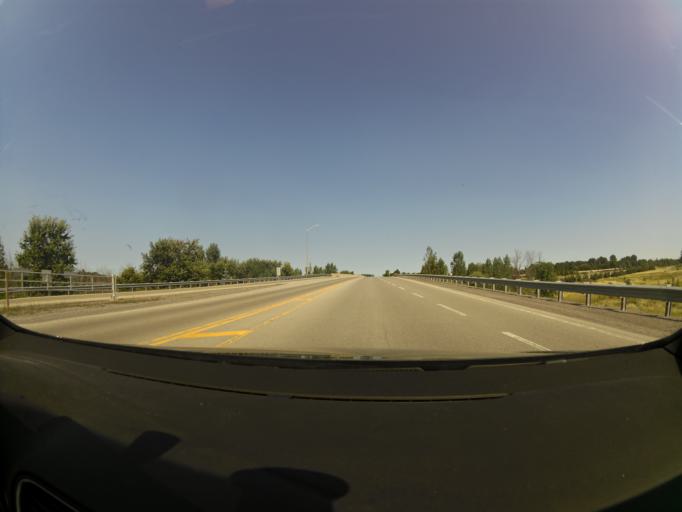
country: CA
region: Ontario
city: Arnprior
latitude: 45.4176
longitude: -76.3301
